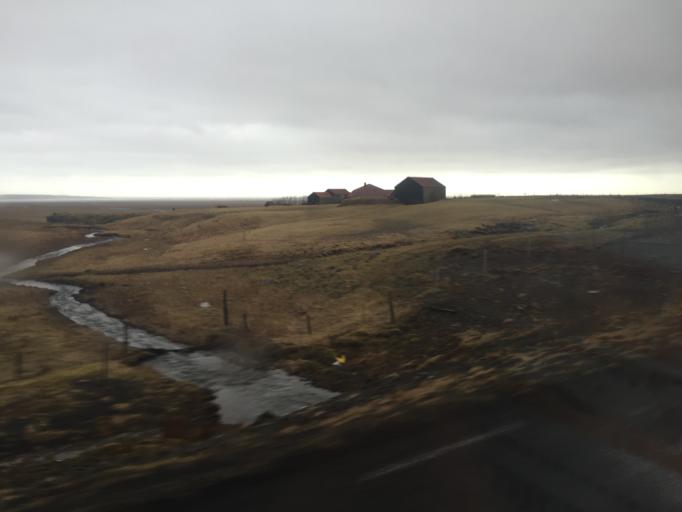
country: IS
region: East
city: Hoefn
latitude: 63.8807
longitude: -16.6397
